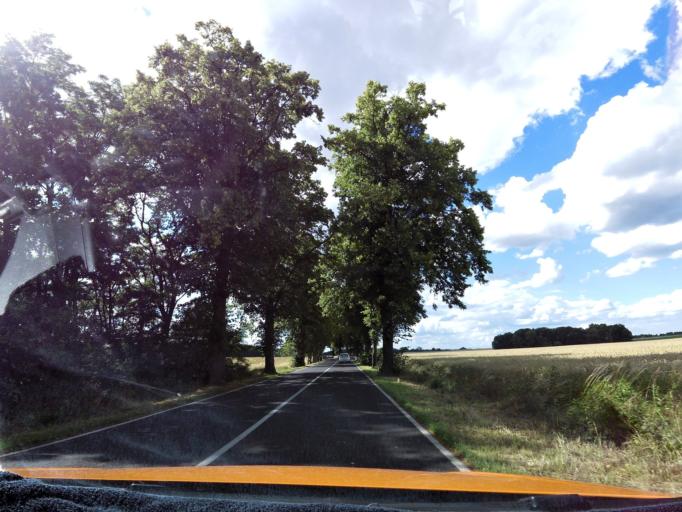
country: DE
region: Brandenburg
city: Mittenwalde
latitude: 52.2999
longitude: 13.5259
